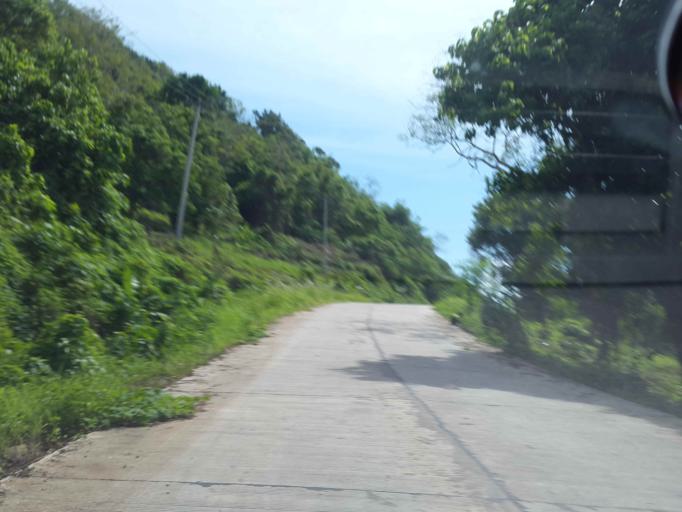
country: ID
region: Banten
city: Citeureup
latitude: -6.5074
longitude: 105.6386
